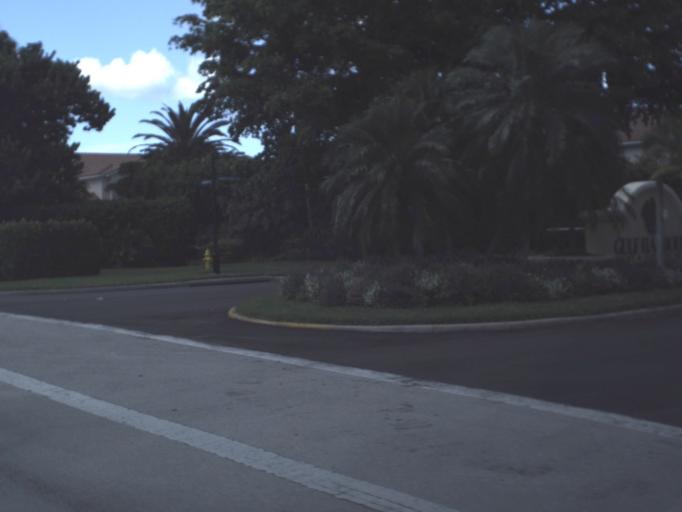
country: US
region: Florida
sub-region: Lee County
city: Harlem Heights
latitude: 26.5213
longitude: -81.9401
